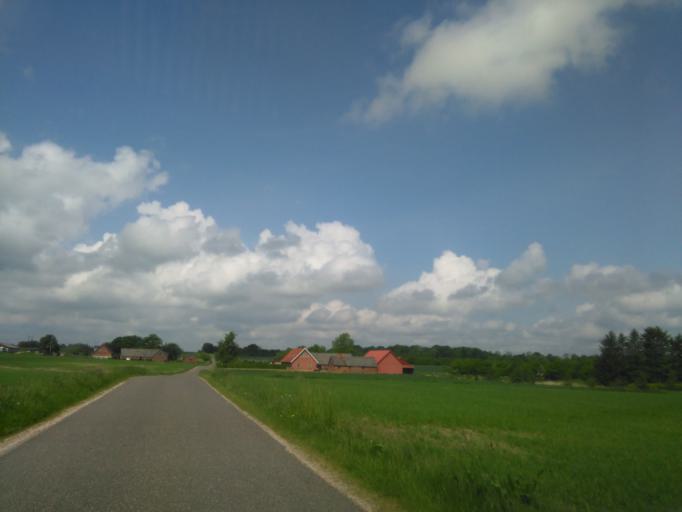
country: DK
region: Central Jutland
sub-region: Skanderborg Kommune
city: Skovby
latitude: 56.2040
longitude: 9.9558
